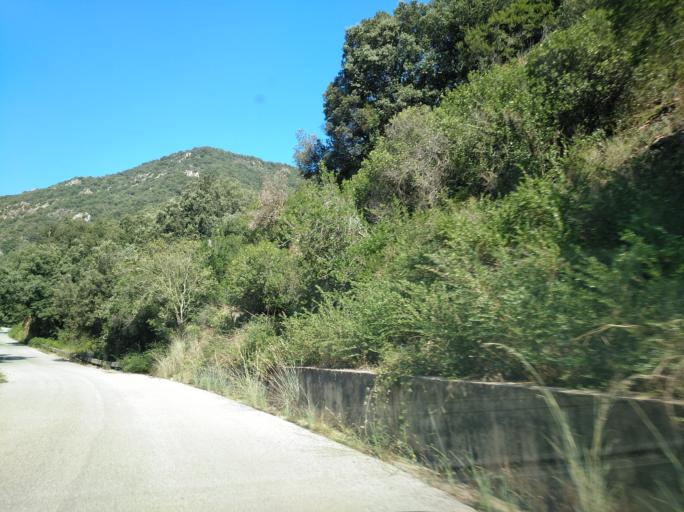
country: ES
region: Catalonia
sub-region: Provincia de Girona
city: Susqueda
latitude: 41.9851
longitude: 2.5376
